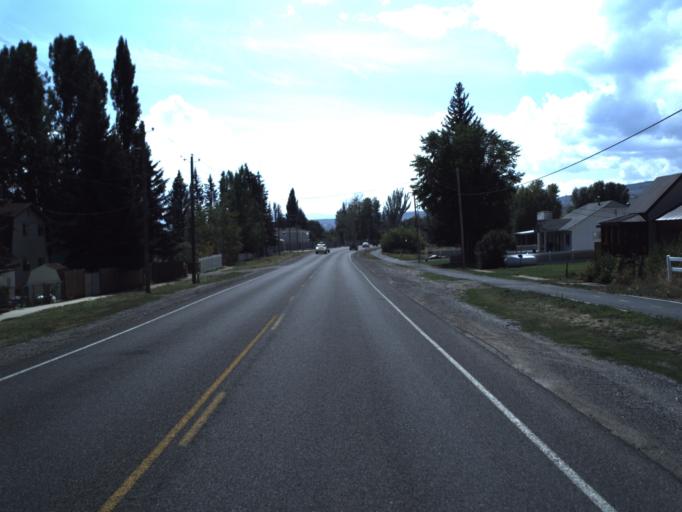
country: US
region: Idaho
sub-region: Bear Lake County
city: Paris
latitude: 41.9386
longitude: -111.3936
